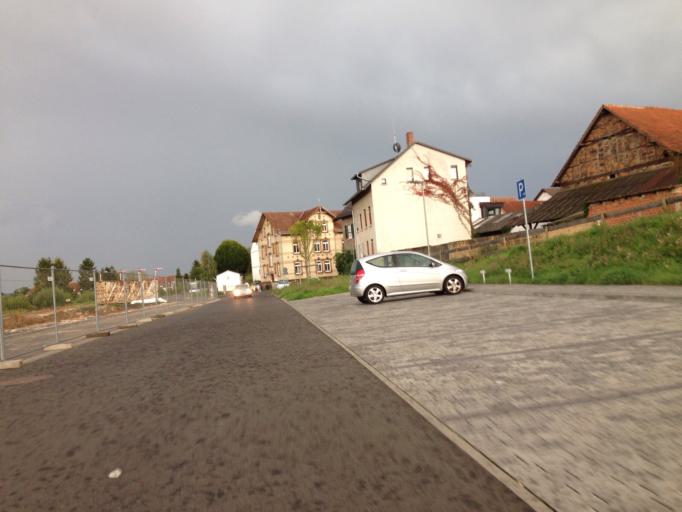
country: DE
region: Hesse
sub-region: Regierungsbezirk Giessen
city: Hungen
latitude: 50.4777
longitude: 8.8930
